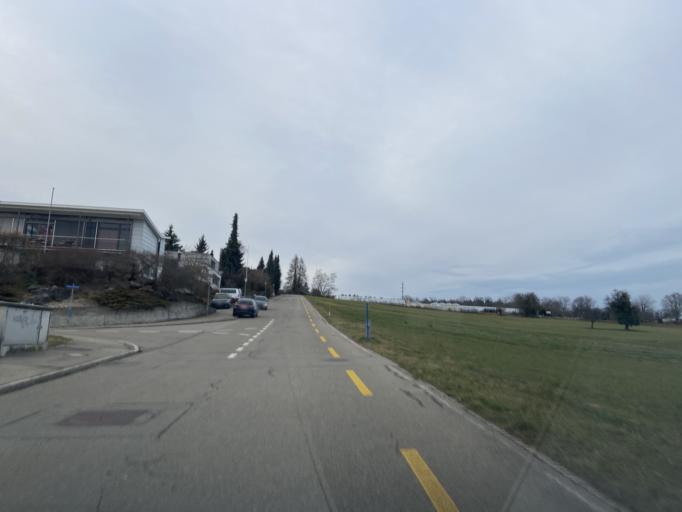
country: CH
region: Zurich
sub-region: Bezirk Winterthur
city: Brutten
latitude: 47.4726
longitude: 8.6837
